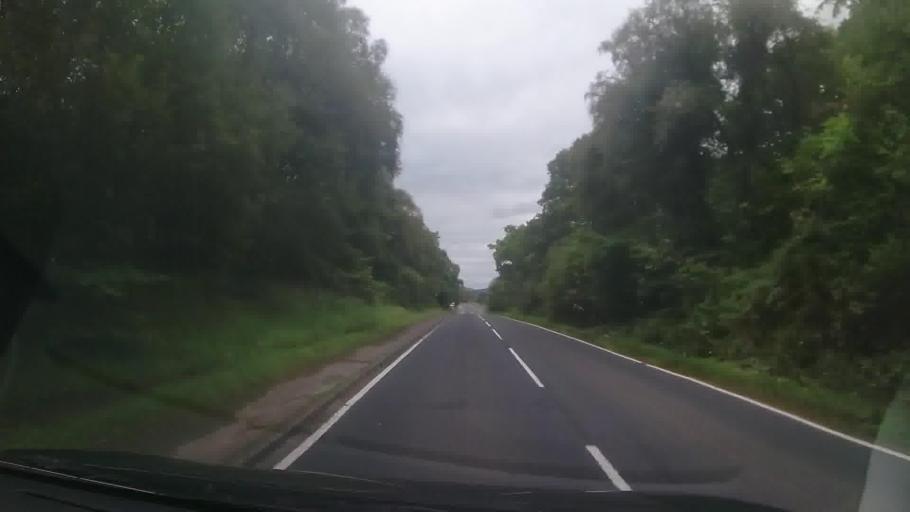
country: GB
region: Scotland
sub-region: Argyll and Bute
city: Garelochhead
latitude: 56.2211
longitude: -5.0347
